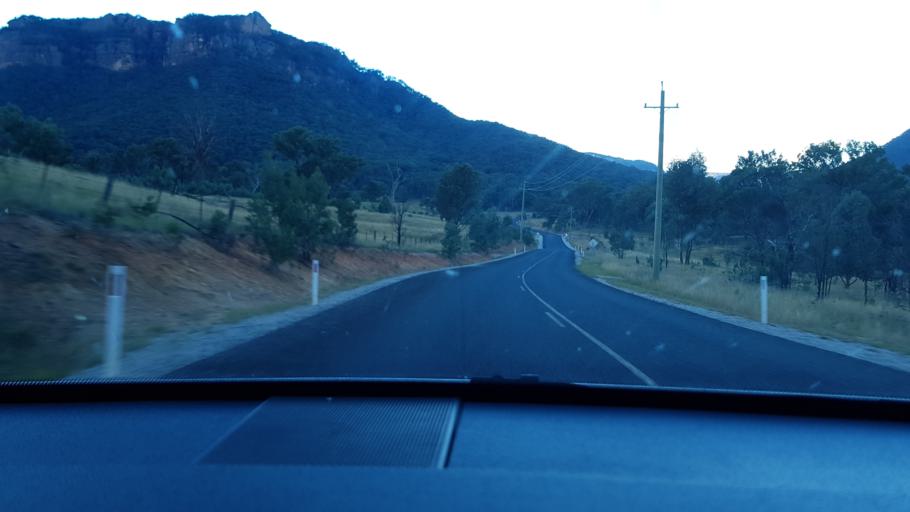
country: AU
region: New South Wales
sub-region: Lithgow
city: Portland
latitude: -33.2398
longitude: 150.1539
